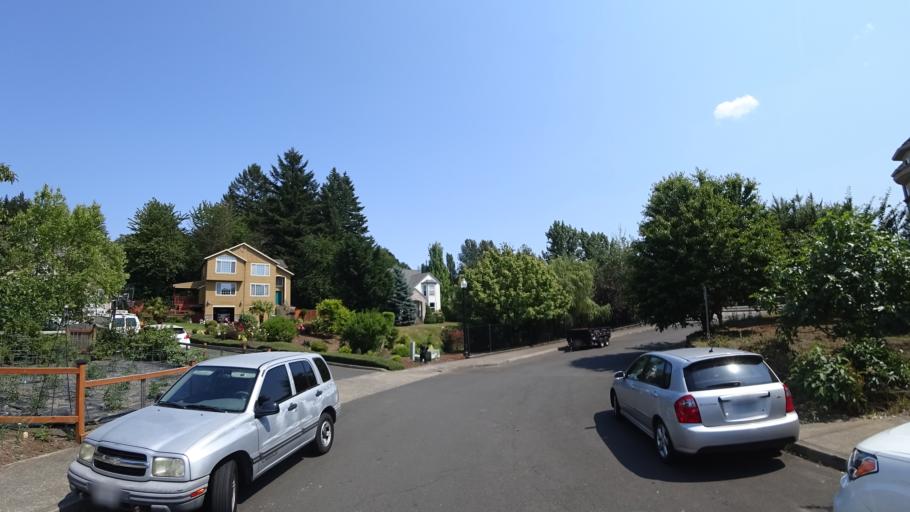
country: US
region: Oregon
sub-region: Clackamas County
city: Happy Valley
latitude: 45.4419
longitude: -122.5622
